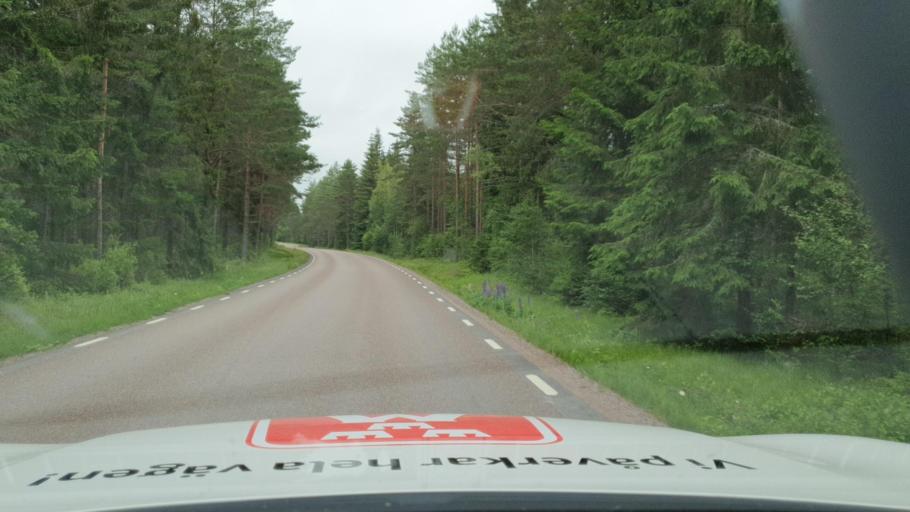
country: SE
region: Vaermland
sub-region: Kristinehamns Kommun
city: Kristinehamn
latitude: 59.4211
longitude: 13.9073
